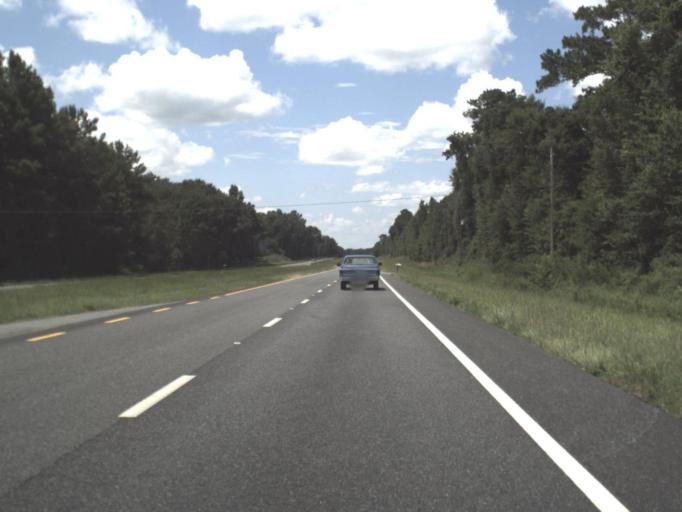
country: US
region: Florida
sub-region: Jefferson County
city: Monticello
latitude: 30.3531
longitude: -83.7952
